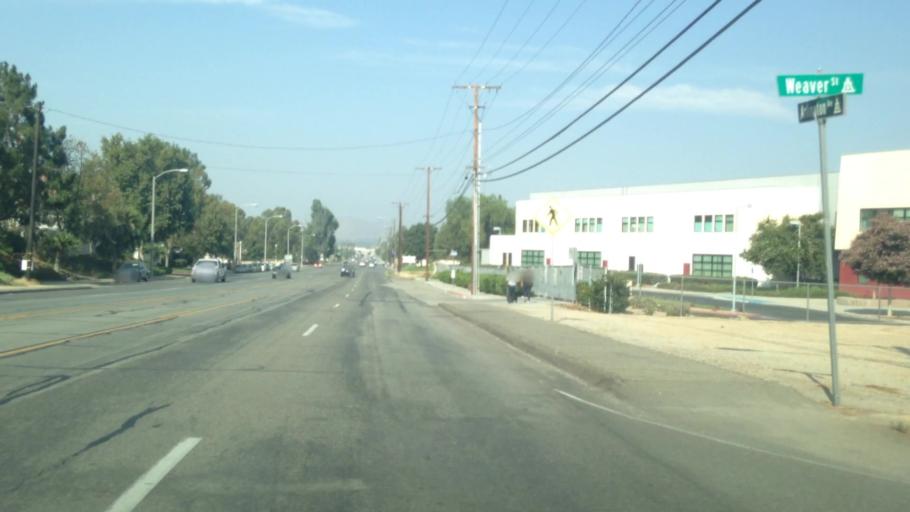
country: US
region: California
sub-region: Riverside County
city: Riverside
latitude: 33.9460
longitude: -117.4396
